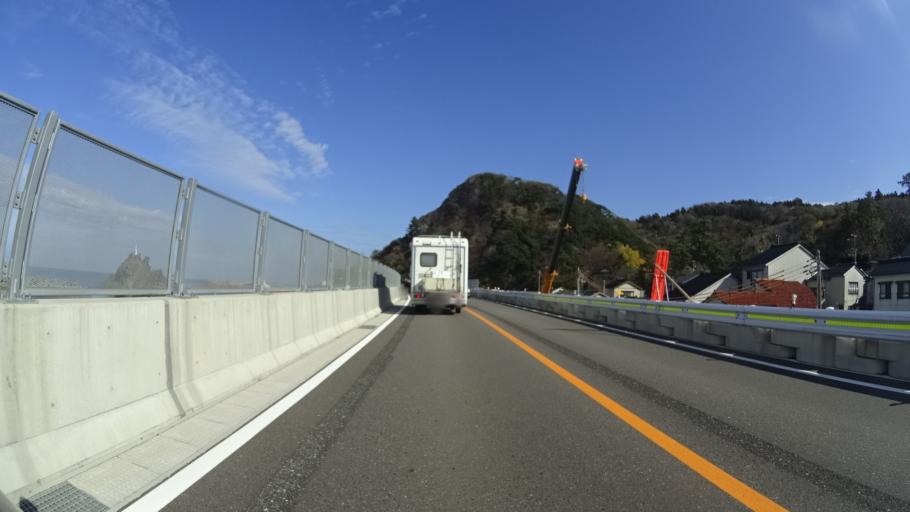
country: JP
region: Niigata
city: Itoigawa
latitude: 37.1065
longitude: 137.9920
